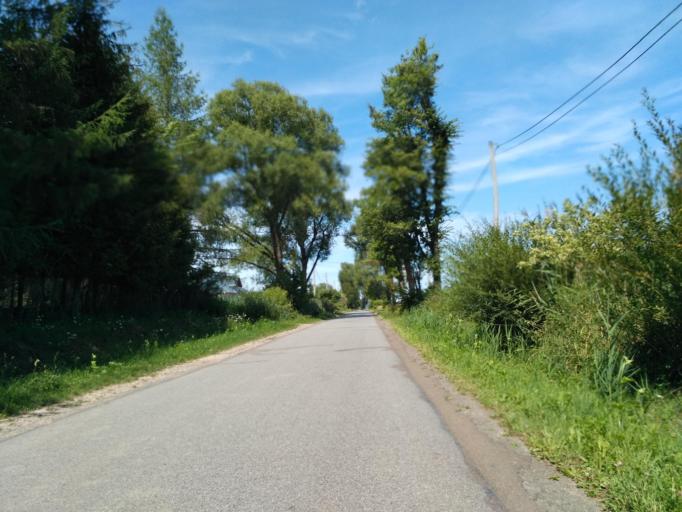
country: PL
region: Subcarpathian Voivodeship
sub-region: Powiat sanocki
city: Strachocina
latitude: 49.5686
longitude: 22.1208
